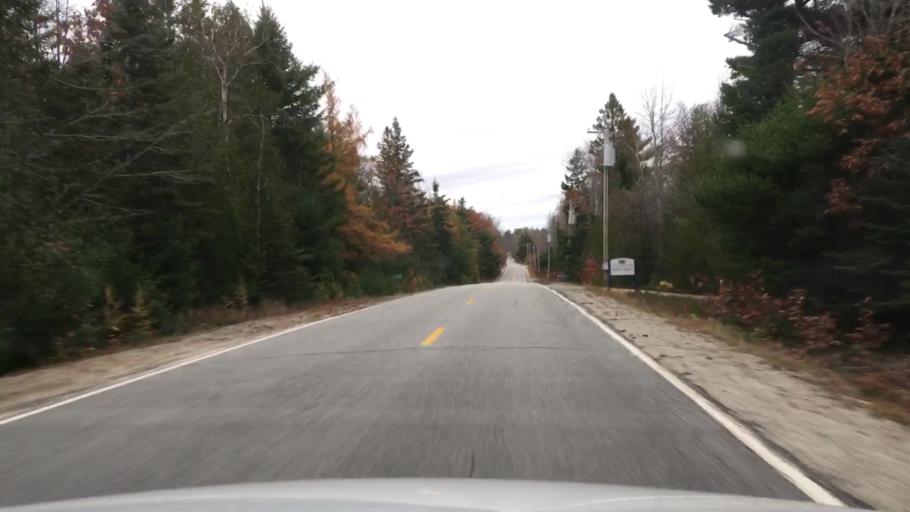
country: US
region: Maine
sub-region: Hancock County
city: Sedgwick
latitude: 44.3123
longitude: -68.5706
